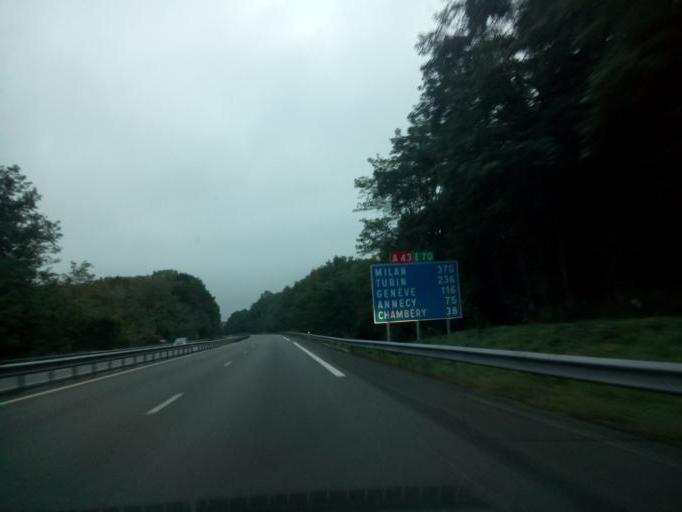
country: FR
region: Rhone-Alpes
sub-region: Departement de l'Isere
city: La Batie-Montgascon
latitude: 45.5640
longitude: 5.5135
